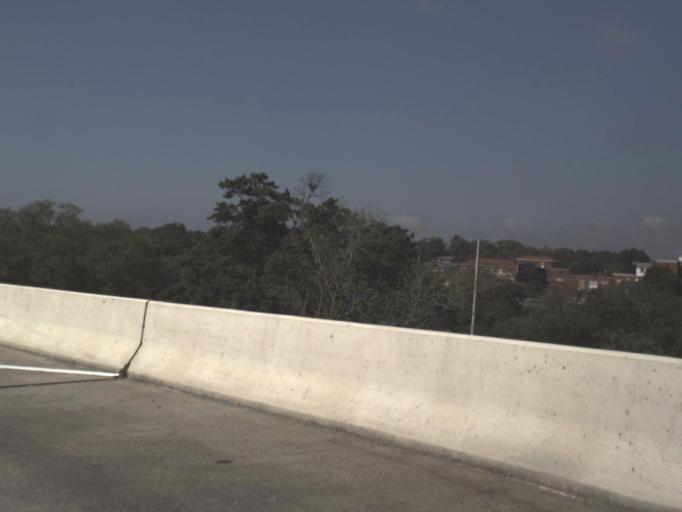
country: US
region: Florida
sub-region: Escambia County
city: Pensacola
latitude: 30.4315
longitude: -87.2161
